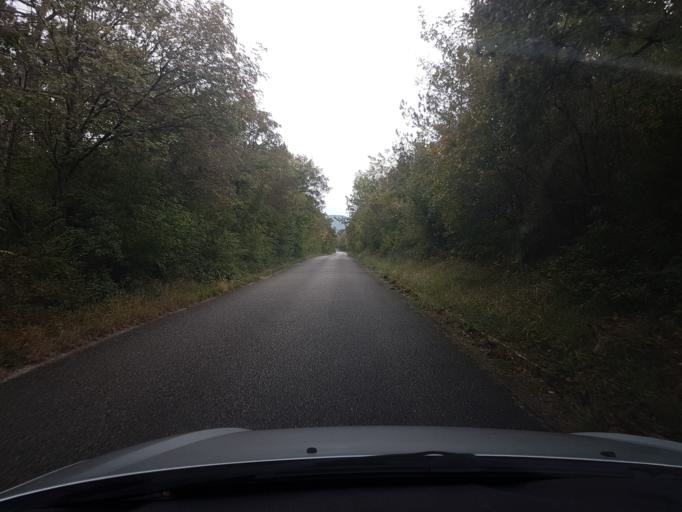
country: IT
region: Friuli Venezia Giulia
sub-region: Provincia di Gorizia
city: Doberdo del Lago
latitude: 45.8313
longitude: 13.5512
